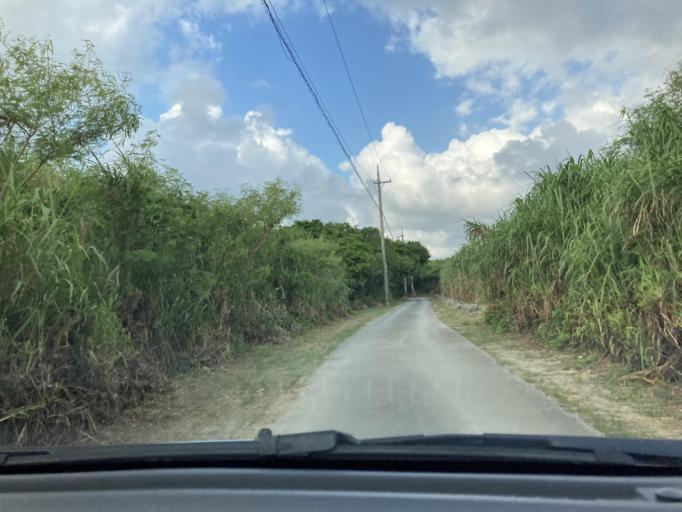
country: JP
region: Okinawa
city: Itoman
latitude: 26.0809
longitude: 127.6690
